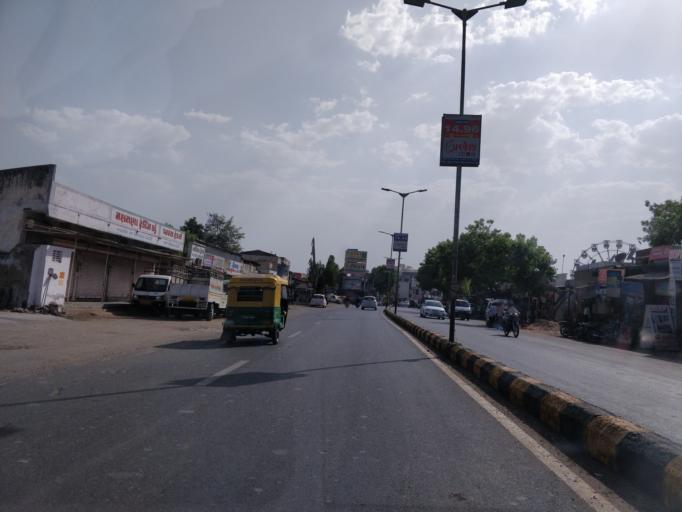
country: IN
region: Gujarat
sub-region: Ahmadabad
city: Naroda
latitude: 23.0754
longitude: 72.6602
